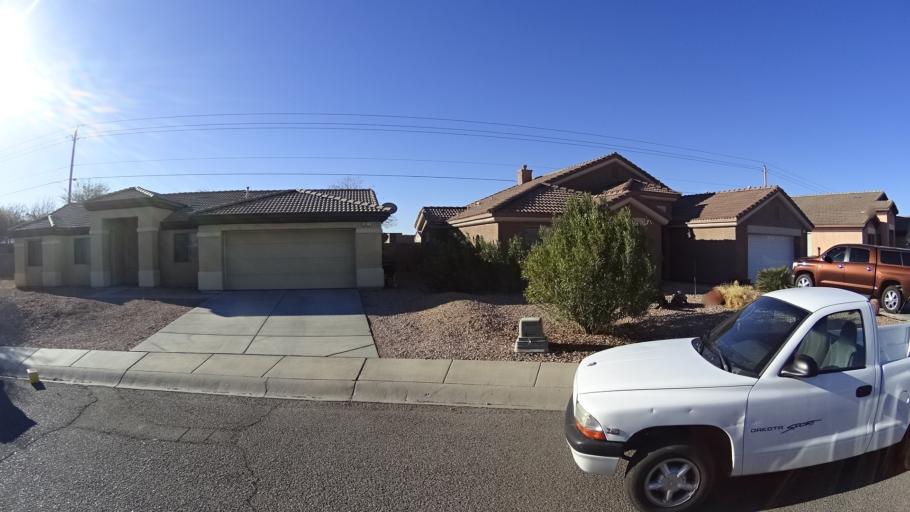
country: US
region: Arizona
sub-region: Mohave County
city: New Kingman-Butler
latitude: 35.2253
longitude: -113.9815
